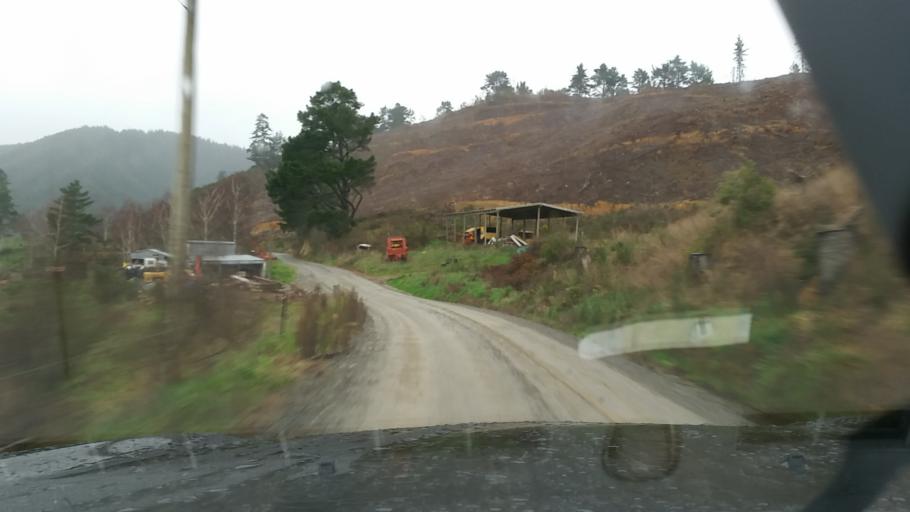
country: NZ
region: Marlborough
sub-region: Marlborough District
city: Picton
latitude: -41.3494
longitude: 173.9297
